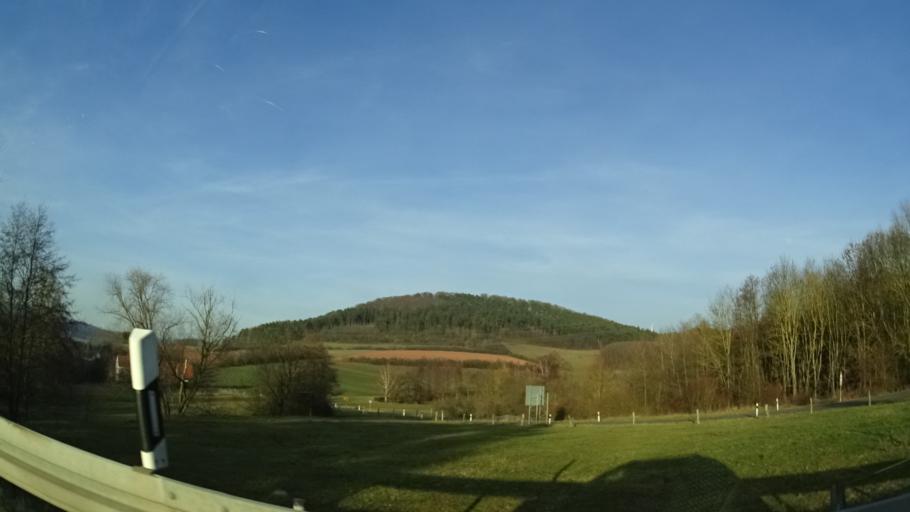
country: DE
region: Hesse
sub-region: Regierungsbezirk Darmstadt
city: Schluchtern
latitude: 50.3261
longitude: 9.5910
